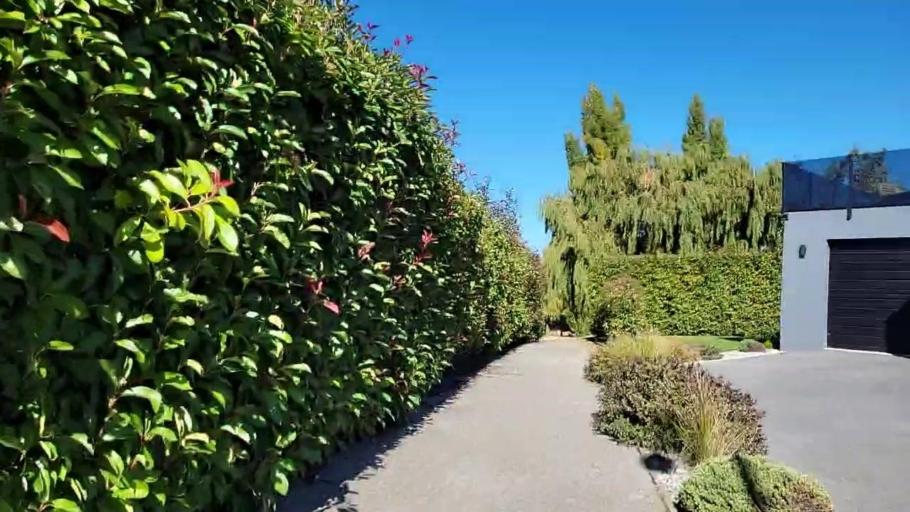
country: NZ
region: Otago
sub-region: Queenstown-Lakes District
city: Wanaka
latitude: -44.9748
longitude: 169.2442
